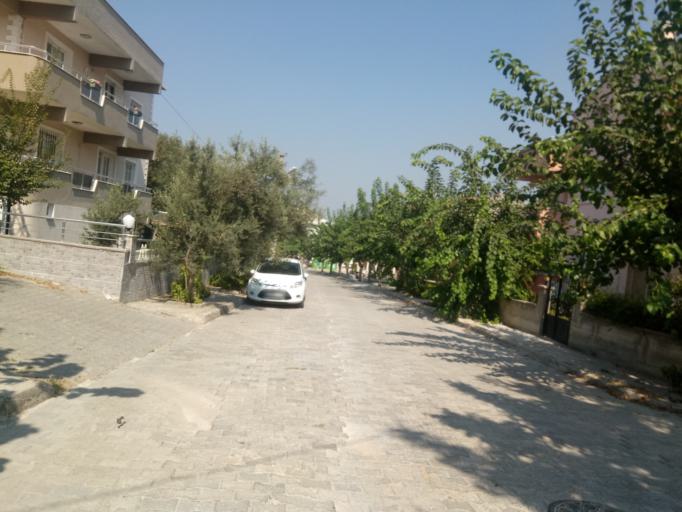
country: TR
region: Izmir
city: Urla
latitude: 38.3266
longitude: 26.7696
